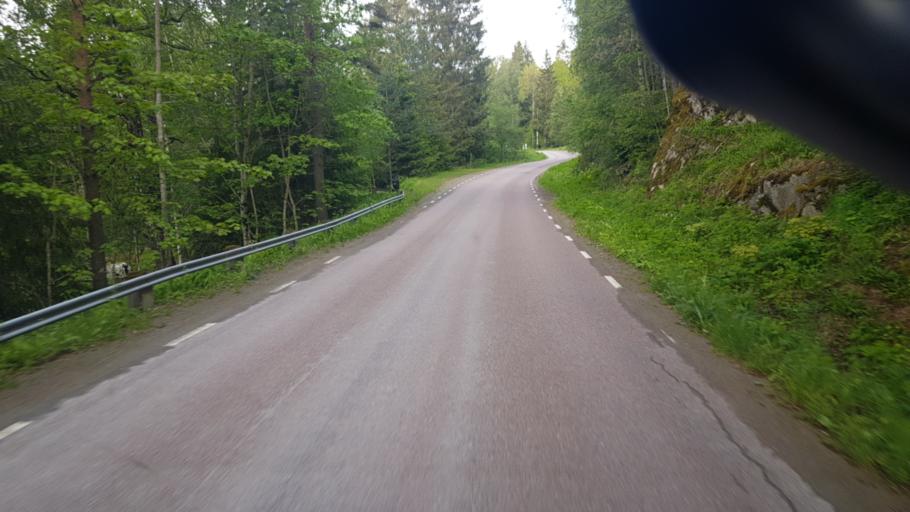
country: NO
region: Hedmark
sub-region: Eidskog
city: Skotterud
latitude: 59.8212
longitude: 12.0044
